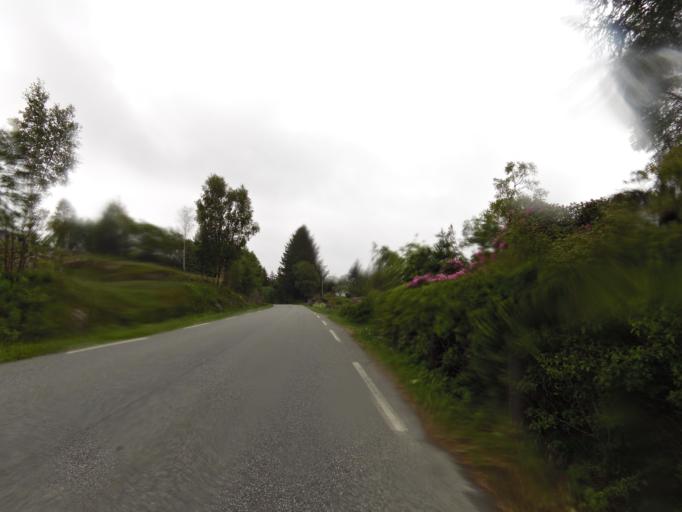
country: NO
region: Hordaland
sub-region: Sveio
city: Sveio
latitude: 59.5241
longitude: 5.2811
